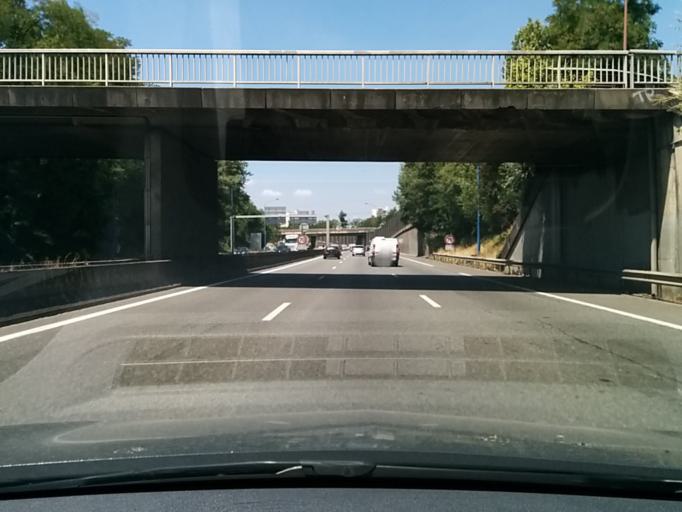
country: FR
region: Midi-Pyrenees
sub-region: Departement de la Haute-Garonne
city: Toulouse
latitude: 43.5752
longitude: 1.4462
